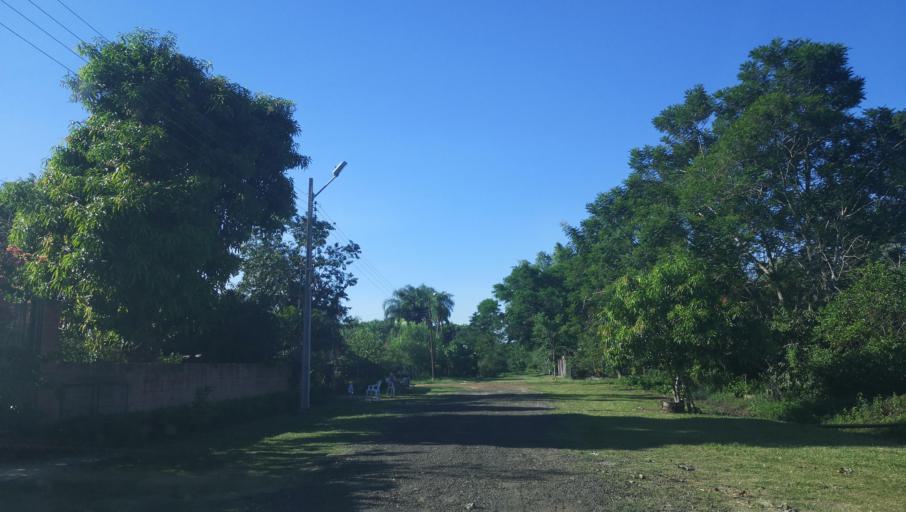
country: PY
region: Caaguazu
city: Carayao
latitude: -25.1953
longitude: -56.3959
